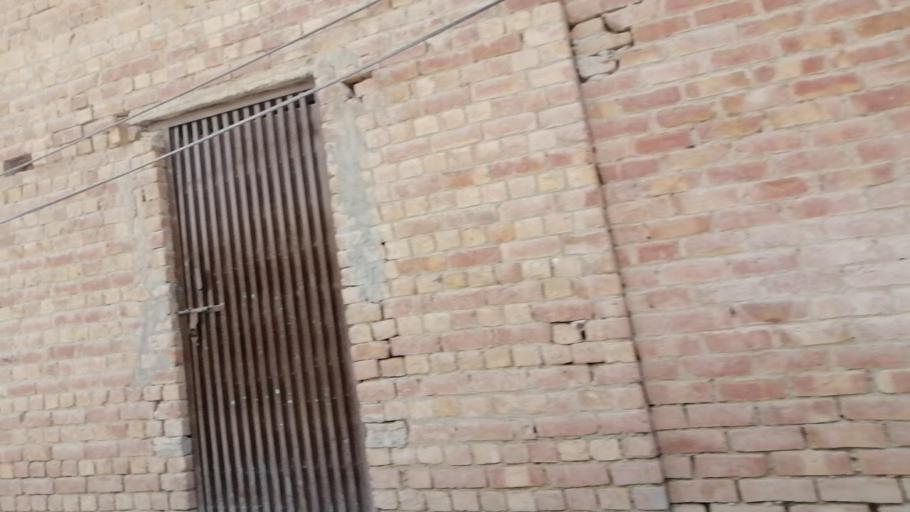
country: PK
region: Punjab
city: Kamalia
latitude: 30.7297
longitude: 72.6564
